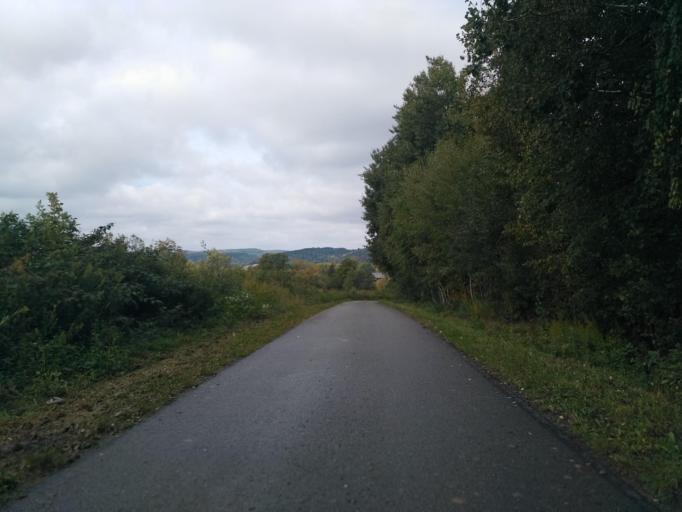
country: PL
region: Subcarpathian Voivodeship
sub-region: Powiat ropczycko-sedziszowski
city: Niedzwiada
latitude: 49.9247
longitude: 21.5051
